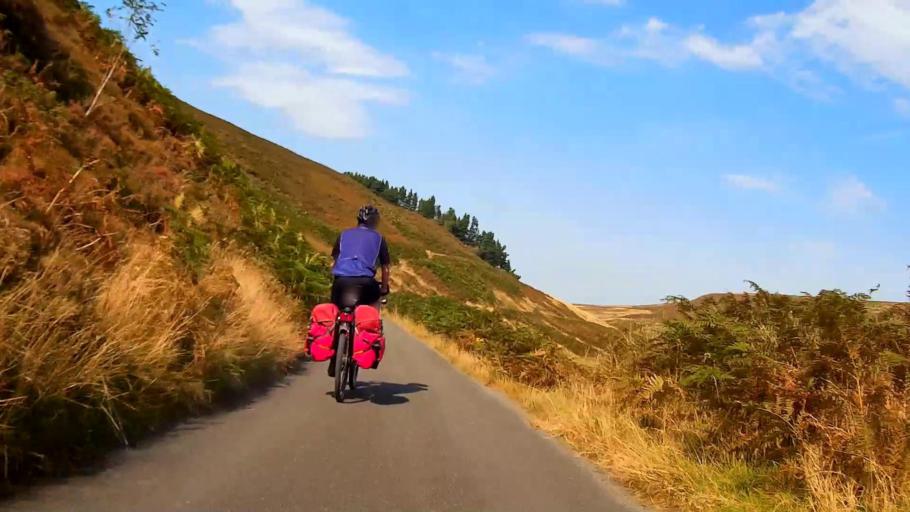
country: GB
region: England
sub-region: Derbyshire
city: Buxton
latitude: 53.2492
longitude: -1.9783
